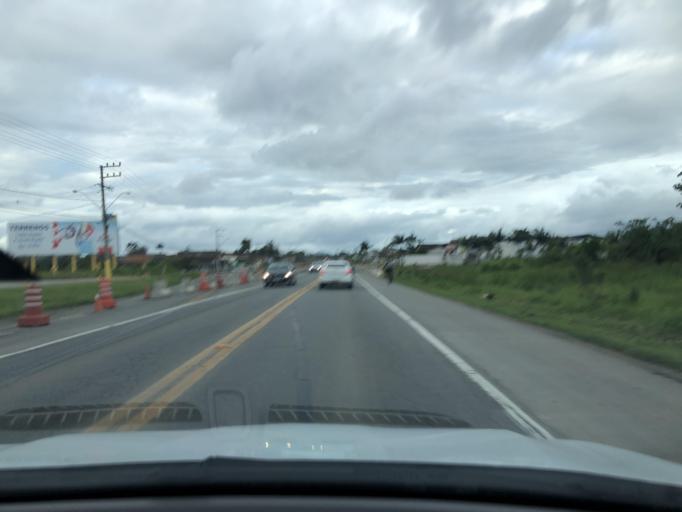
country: BR
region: Santa Catarina
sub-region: Joinville
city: Joinville
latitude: -26.4029
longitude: -48.7444
